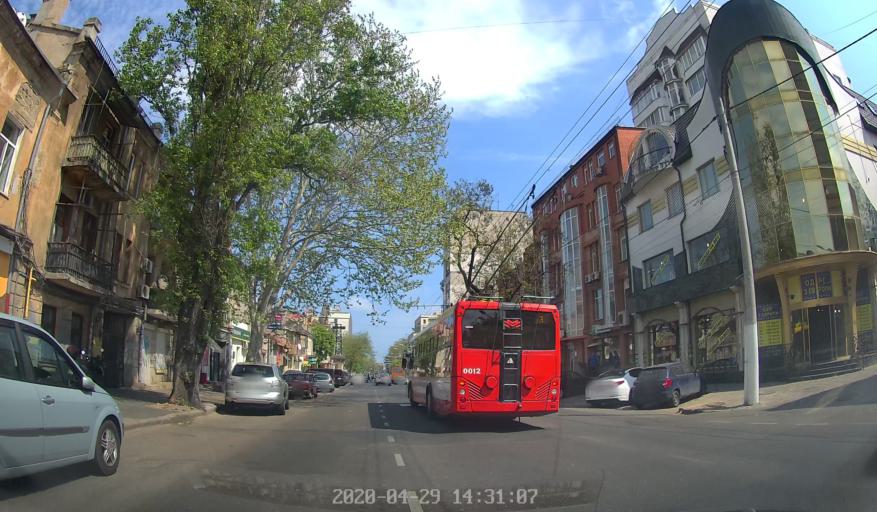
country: NG
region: Niger
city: Lemu
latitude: 9.2943
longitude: 6.1471
